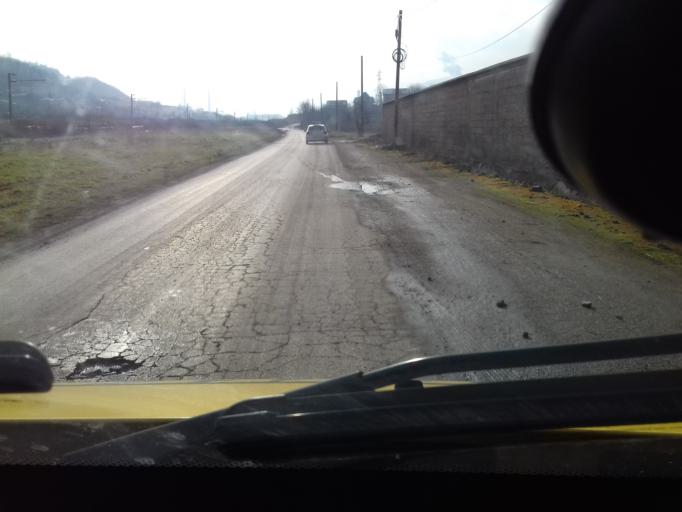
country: BA
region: Federation of Bosnia and Herzegovina
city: Zenica
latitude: 44.2475
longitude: 17.8966
